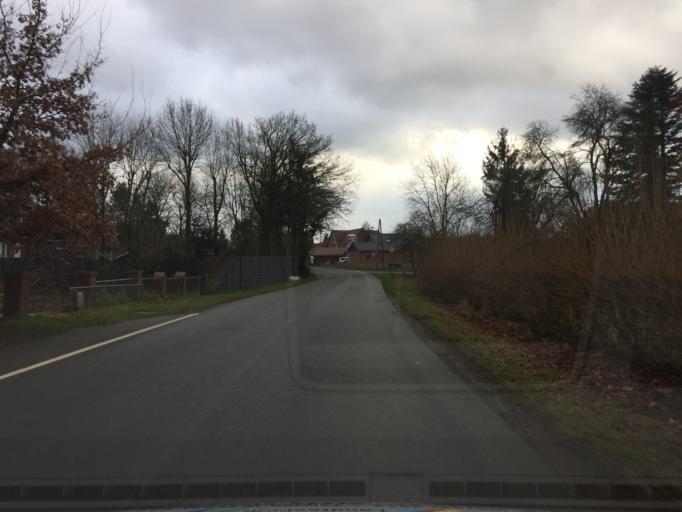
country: DE
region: Lower Saxony
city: Stolzenau
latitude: 52.5239
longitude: 9.0532
